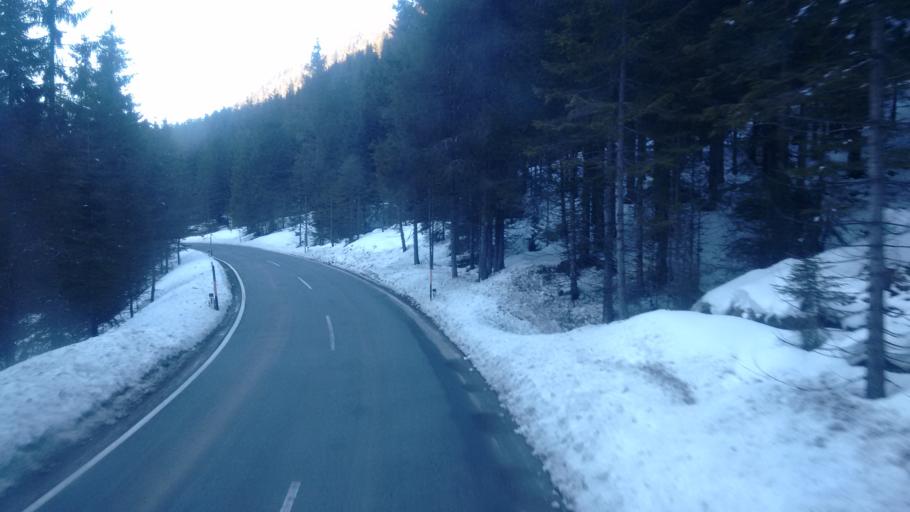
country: AT
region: Salzburg
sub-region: Politischer Bezirk Sankt Johann im Pongau
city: Untertauern
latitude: 47.3138
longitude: 13.4488
